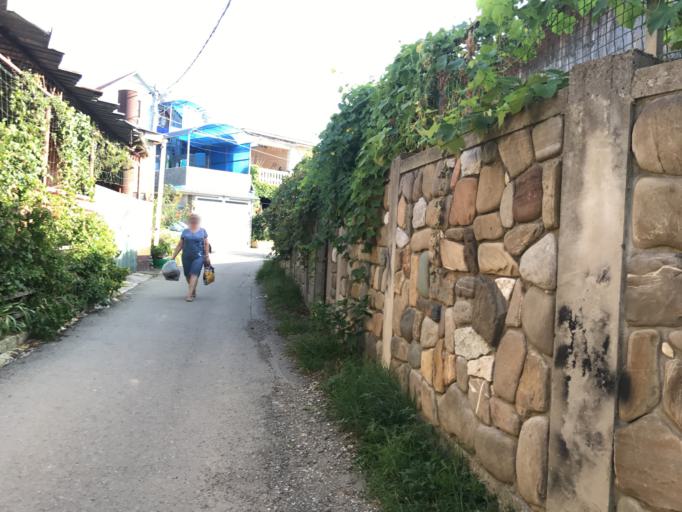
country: RU
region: Krasnodarskiy
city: Adler
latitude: 43.4205
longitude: 39.9400
